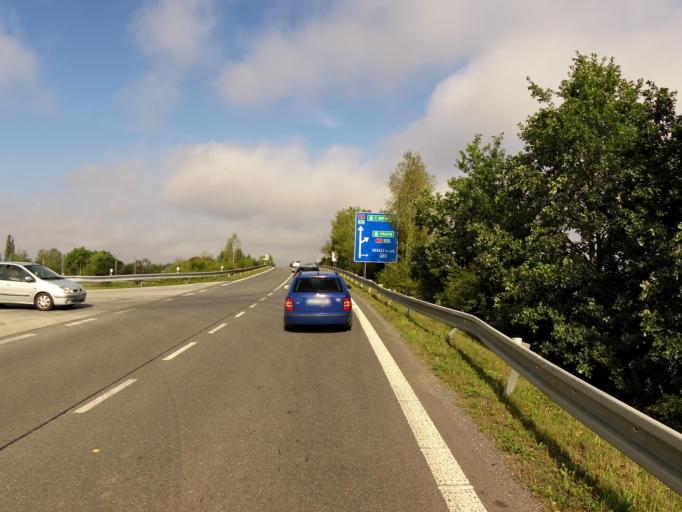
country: CZ
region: Jihocesky
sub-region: Okres Tabor
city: Veseli nad Luznici
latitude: 49.1713
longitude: 14.6834
